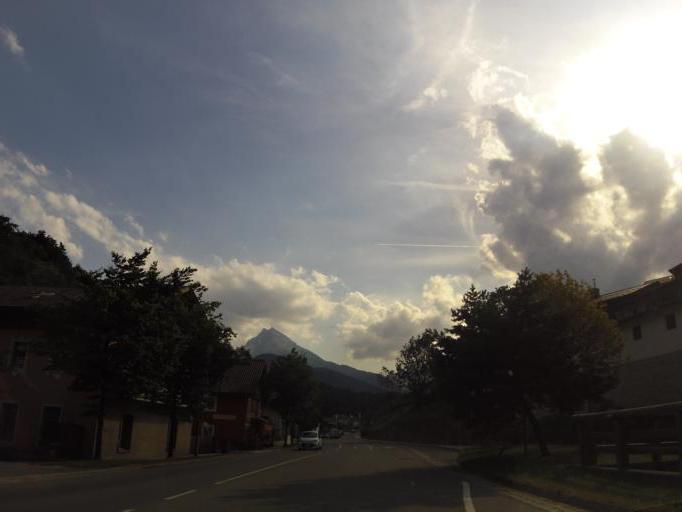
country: DE
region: Bavaria
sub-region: Upper Bavaria
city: Berchtesgaden
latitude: 47.6299
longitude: 13.0052
